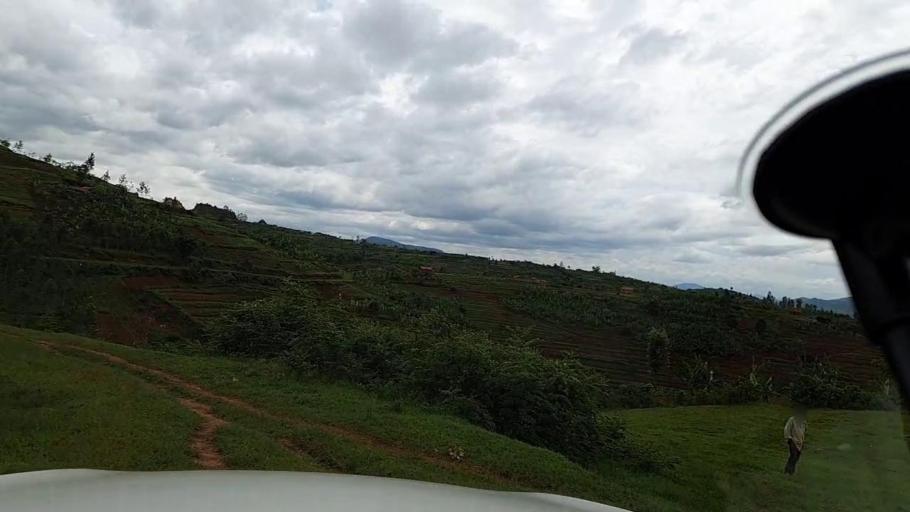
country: RW
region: Southern Province
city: Gitarama
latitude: -2.0745
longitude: 29.6426
